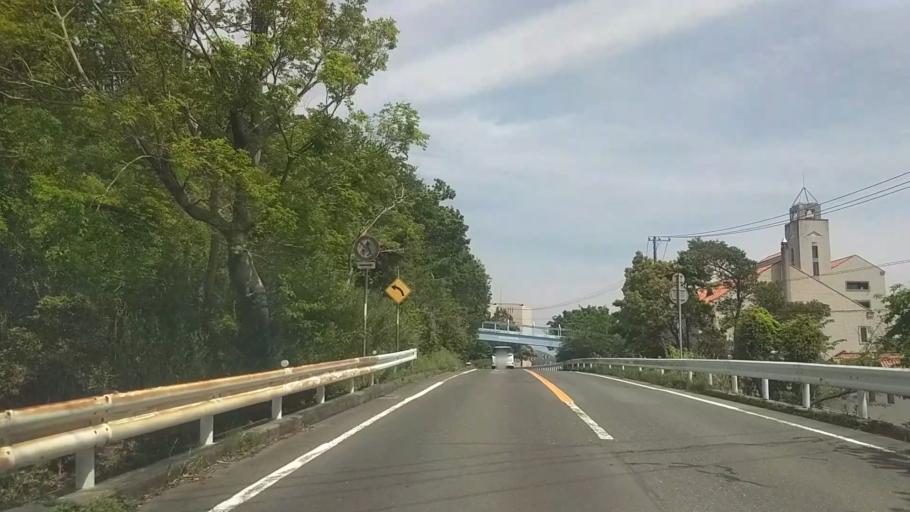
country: JP
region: Shizuoka
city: Kosai-shi
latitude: 34.7827
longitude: 137.5774
